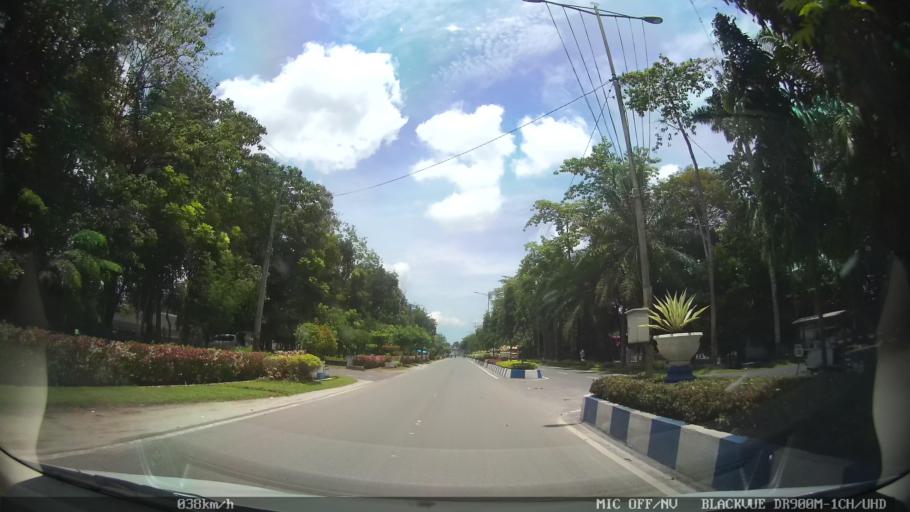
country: ID
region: North Sumatra
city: Percut
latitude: 3.5489
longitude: 98.8654
